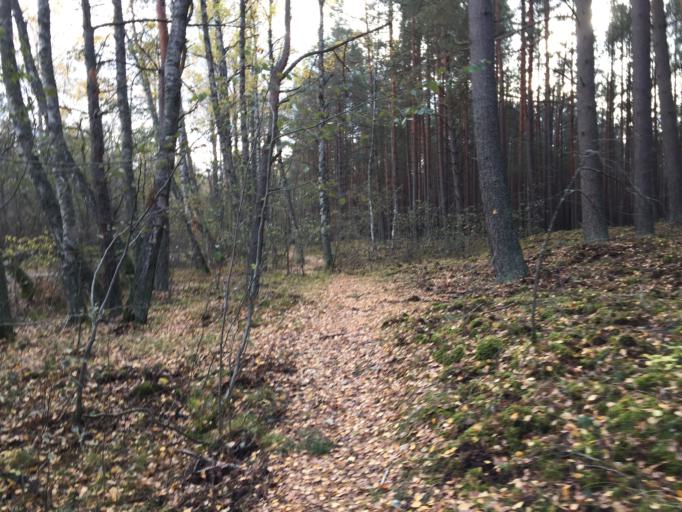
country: LV
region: Carnikava
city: Carnikava
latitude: 57.1464
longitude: 24.2634
